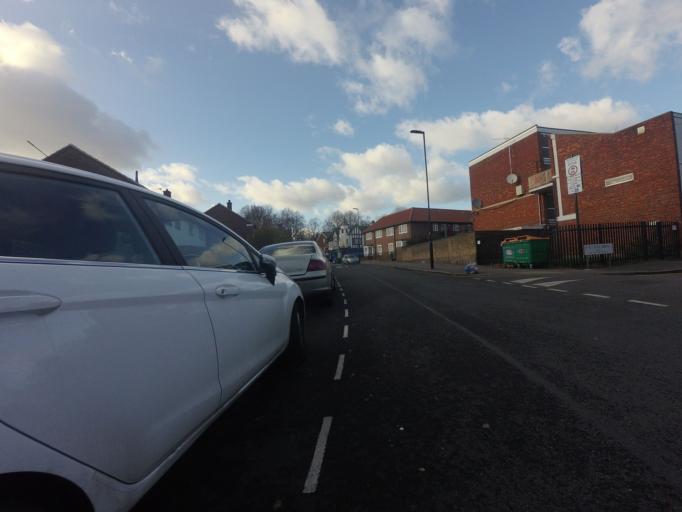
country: GB
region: England
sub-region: Greater London
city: Poplar
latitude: 51.5360
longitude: 0.0110
